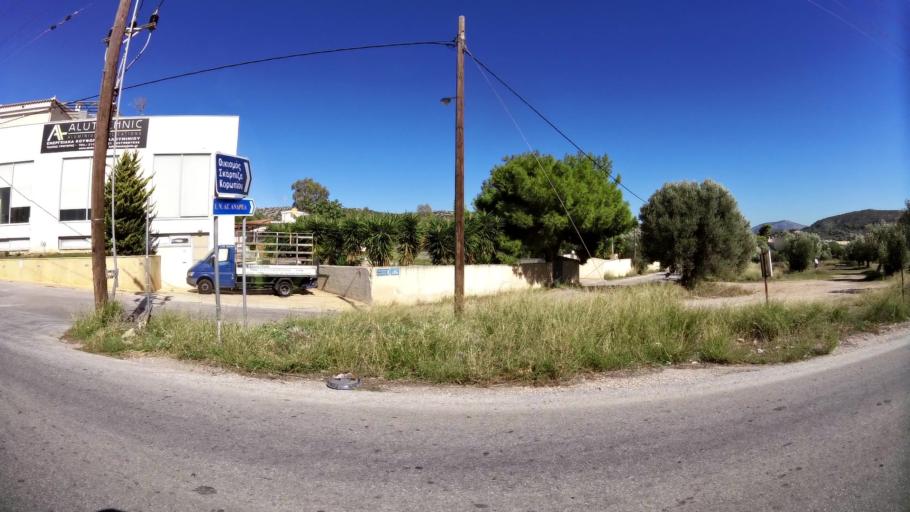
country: GR
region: Attica
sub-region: Nomarchia Anatolikis Attikis
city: Vari
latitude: 37.8455
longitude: 23.8162
